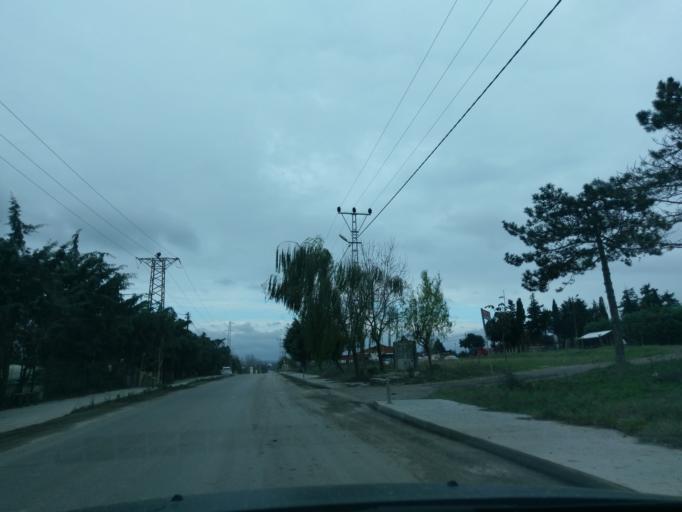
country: TR
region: Istanbul
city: Catalca
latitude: 41.1892
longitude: 28.4024
